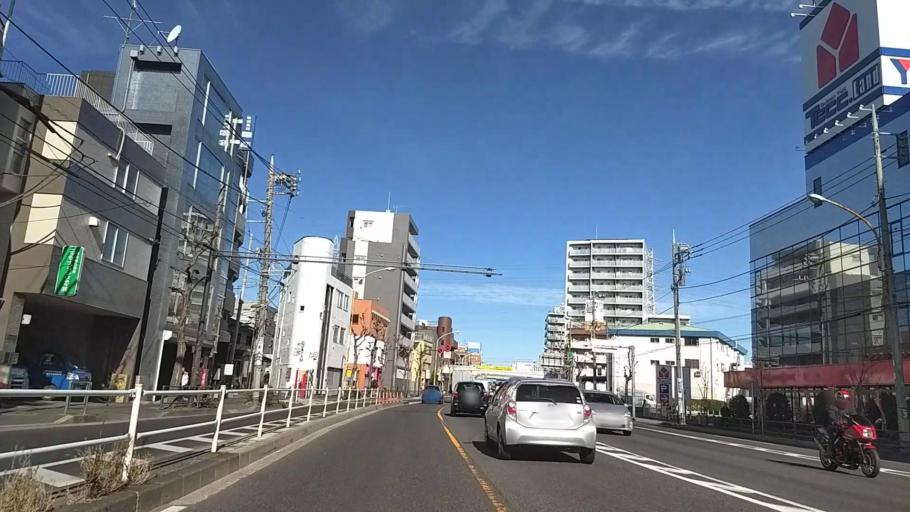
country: JP
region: Tokyo
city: Mitaka-shi
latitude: 35.6733
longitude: 139.6135
